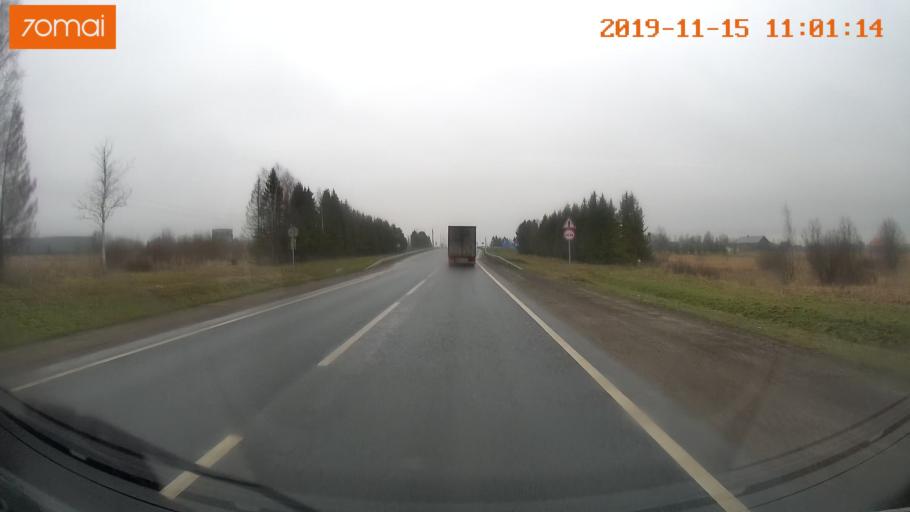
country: RU
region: Vologda
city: Chebsara
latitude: 59.1337
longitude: 38.9165
